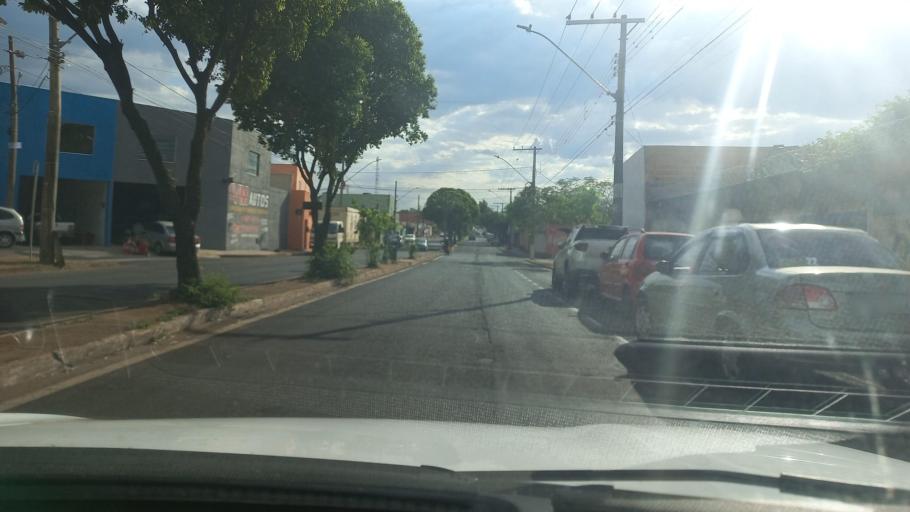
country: BR
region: Minas Gerais
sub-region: Uberaba
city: Uberaba
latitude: -19.7602
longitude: -47.9112
